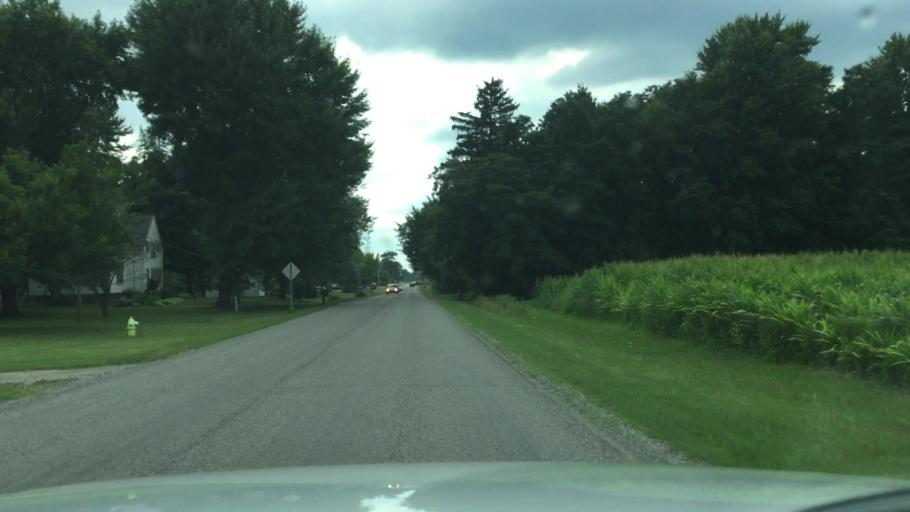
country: US
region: Michigan
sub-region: Saginaw County
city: Bridgeport
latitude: 43.3215
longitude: -83.8185
